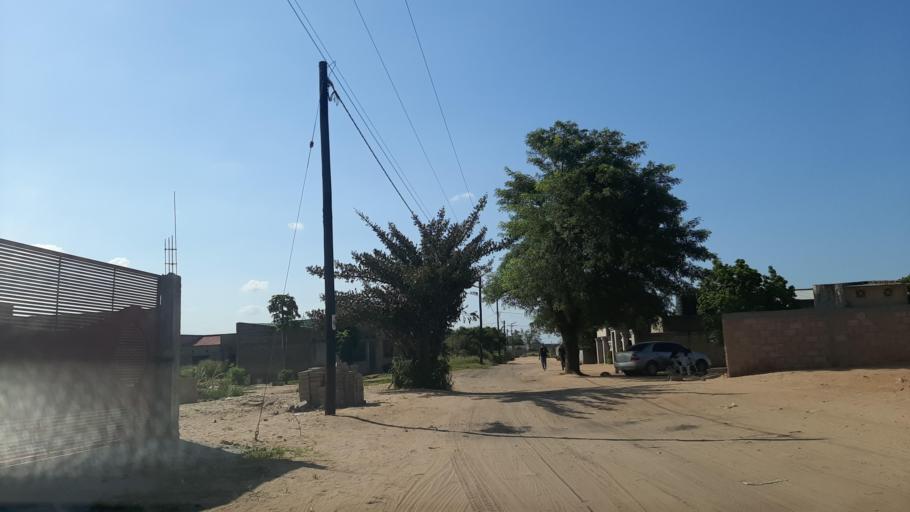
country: MZ
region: Maputo
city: Matola
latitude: -25.8069
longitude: 32.4914
